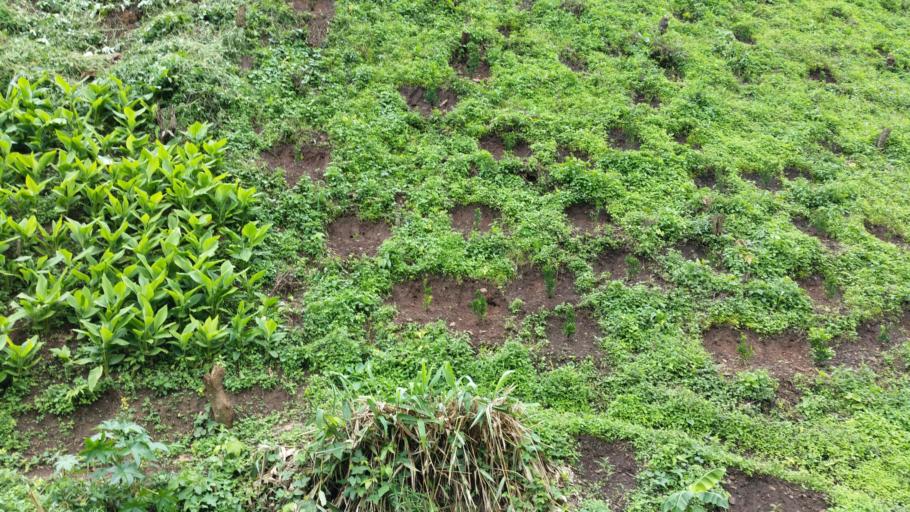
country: MM
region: Mandalay
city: Yamethin
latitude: 20.6219
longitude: 96.5213
